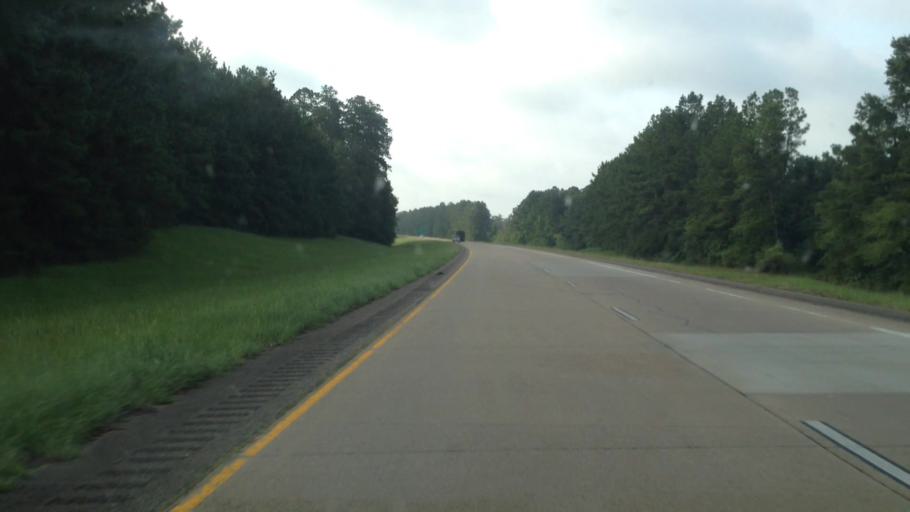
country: US
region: Louisiana
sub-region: Rapides Parish
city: Lecompte
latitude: 31.0356
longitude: -92.4135
